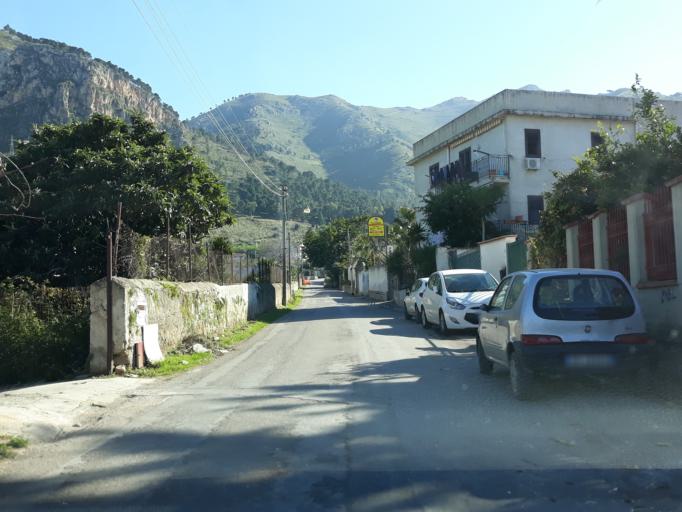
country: IT
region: Sicily
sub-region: Palermo
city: Villa Ciambra
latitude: 38.0787
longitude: 13.3468
